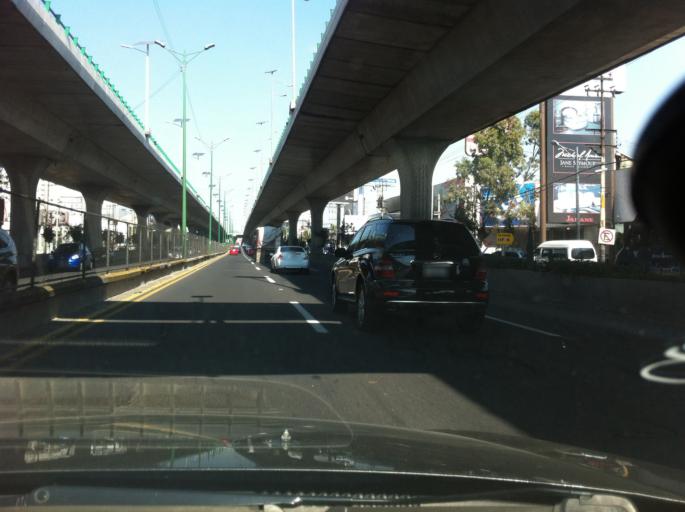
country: MX
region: Mexico
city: Naucalpan de Juarez
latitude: 19.4631
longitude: -99.2233
